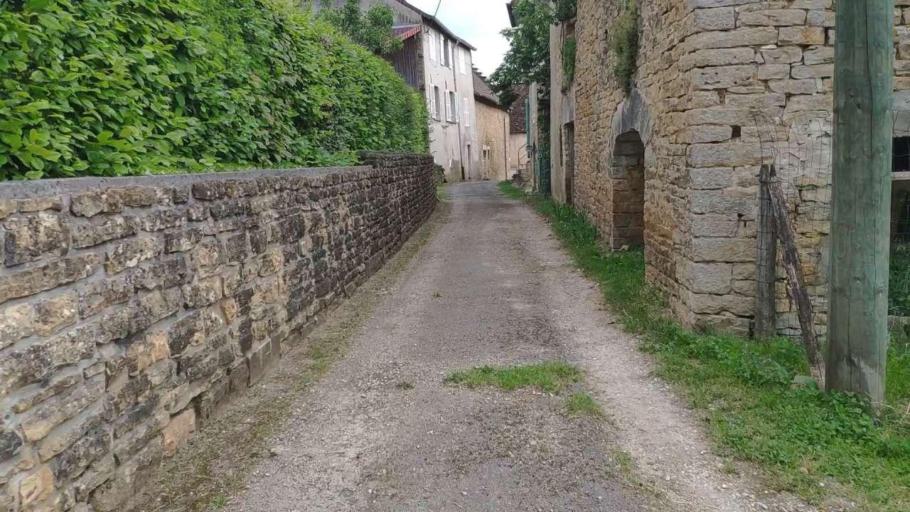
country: FR
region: Franche-Comte
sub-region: Departement du Jura
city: Bletterans
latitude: 46.7856
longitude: 5.5644
